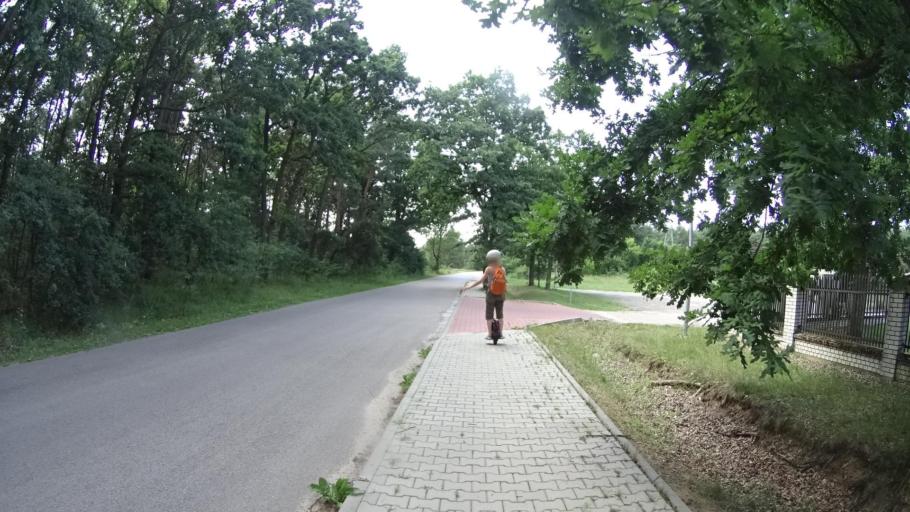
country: PL
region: Masovian Voivodeship
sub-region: Powiat bialobrzeski
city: Bialobrzegi
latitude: 51.6445
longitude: 20.9665
